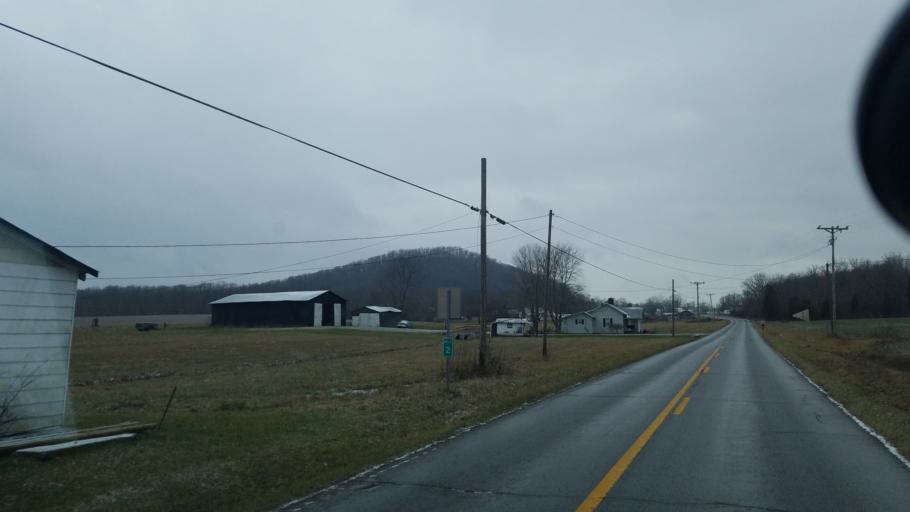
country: US
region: Kentucky
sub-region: Fleming County
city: Flemingsburg
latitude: 38.4759
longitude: -83.5963
